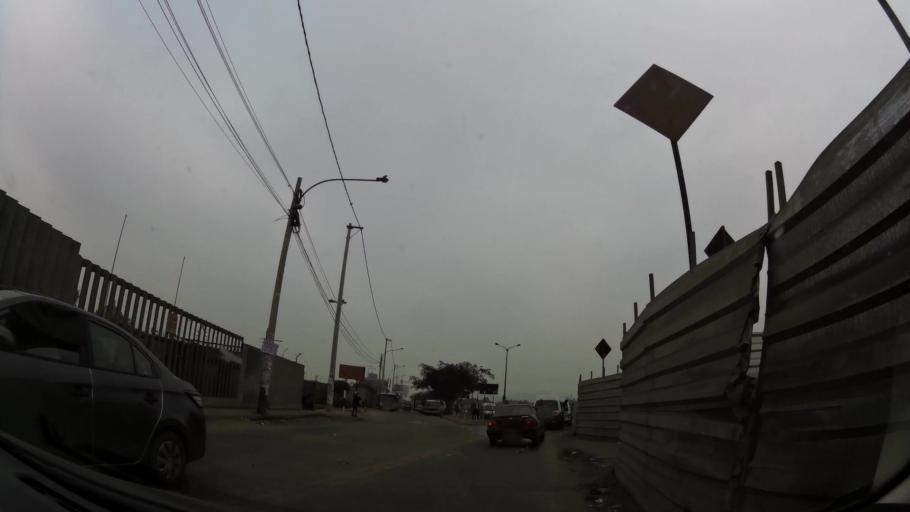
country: PE
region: Lima
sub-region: Lima
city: Vitarte
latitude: -12.0452
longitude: -76.9409
